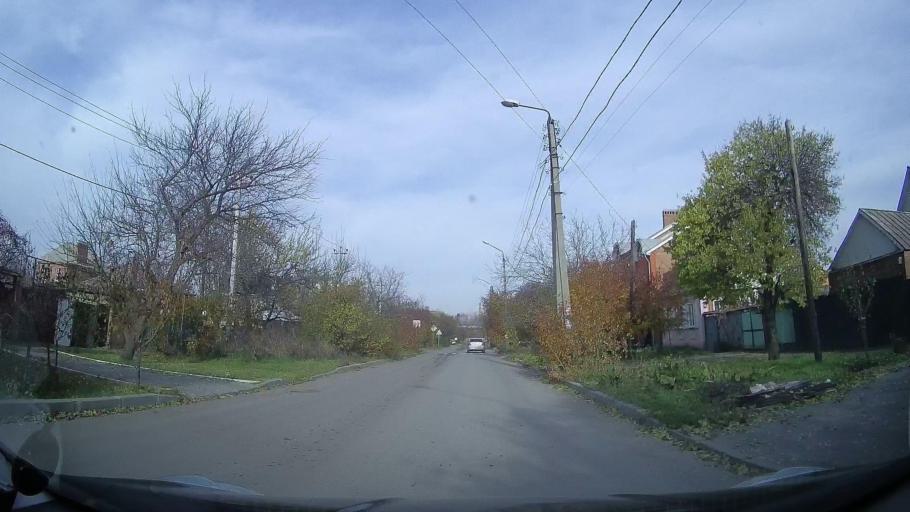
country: RU
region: Rostov
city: Severnyy
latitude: 47.2634
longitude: 39.7238
